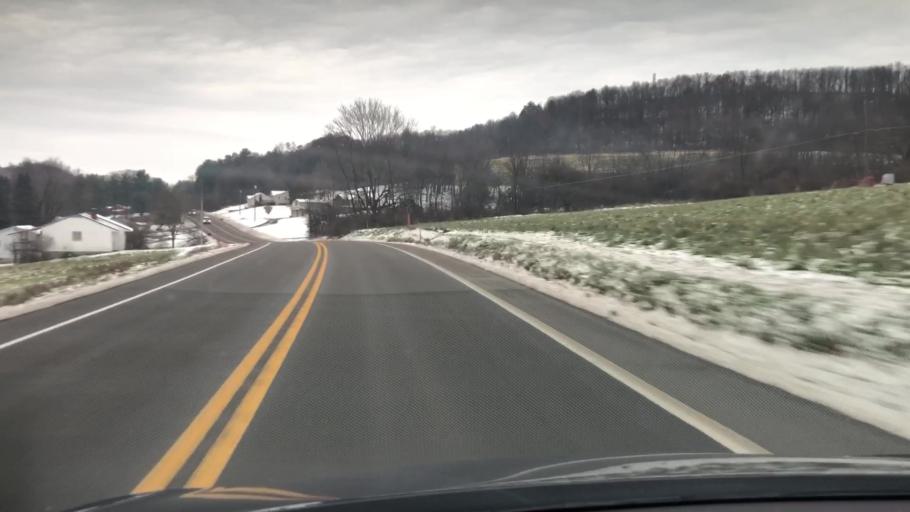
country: US
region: Pennsylvania
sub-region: Jefferson County
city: Brookville
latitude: 41.0425
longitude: -79.2549
